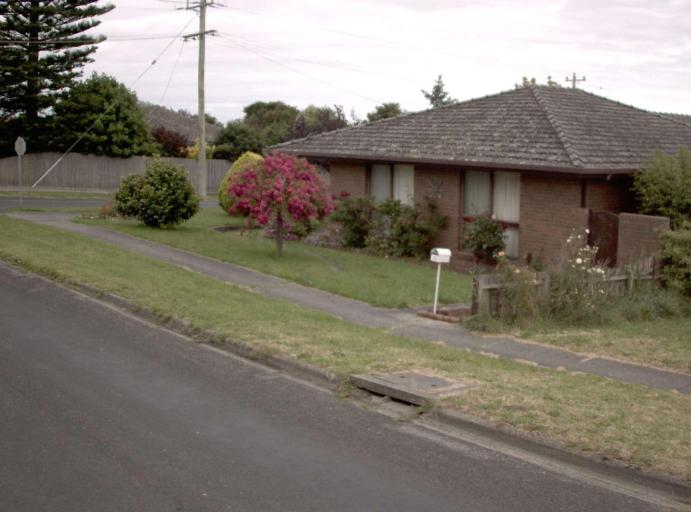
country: AU
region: Victoria
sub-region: Bass Coast
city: North Wonthaggi
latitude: -38.4374
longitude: 145.8149
